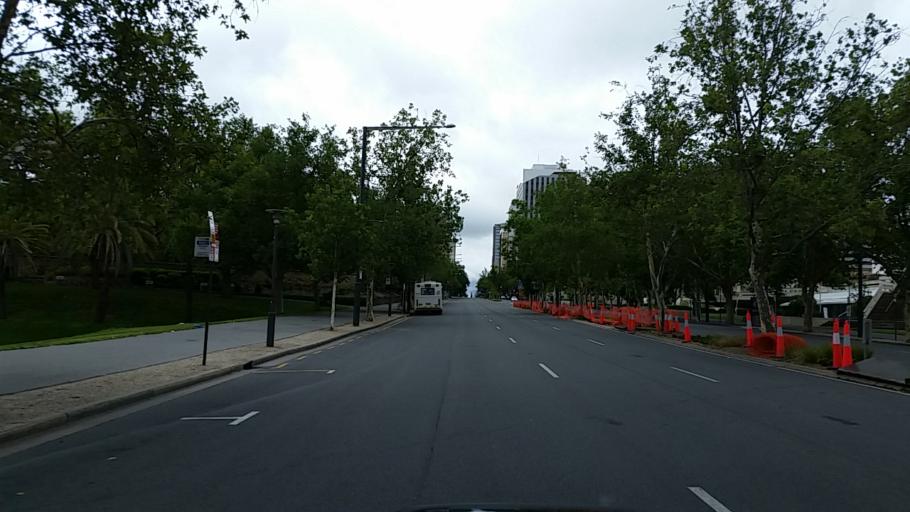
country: AU
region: South Australia
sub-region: Adelaide
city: Adelaide
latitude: -34.9182
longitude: 138.5992
